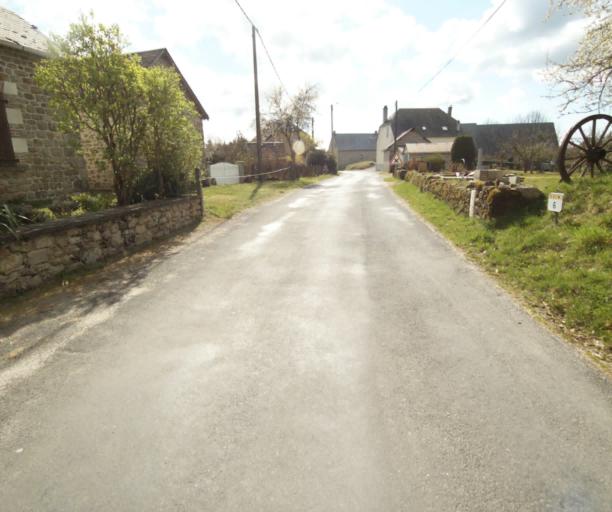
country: FR
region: Limousin
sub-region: Departement de la Correze
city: Correze
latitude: 45.2456
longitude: 1.9502
